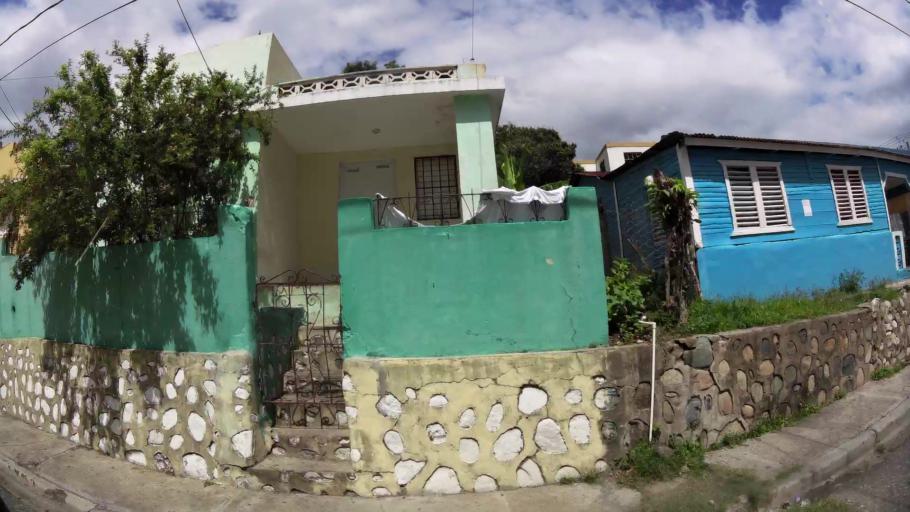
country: DO
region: San Cristobal
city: San Cristobal
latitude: 18.4079
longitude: -70.1126
